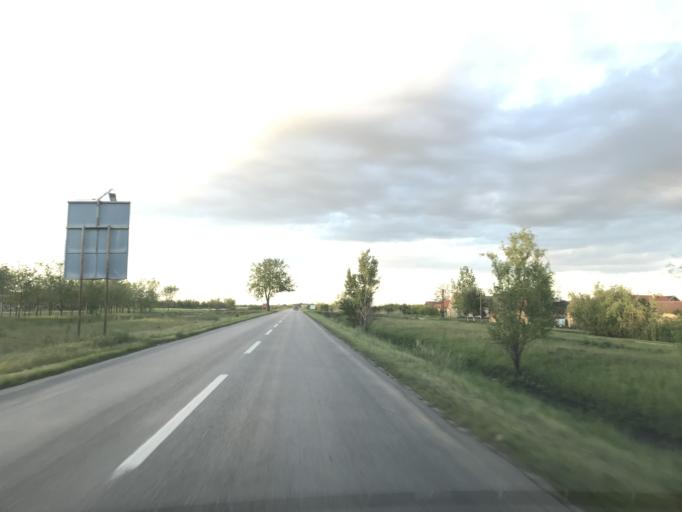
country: RS
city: Banatsko Karadordevo
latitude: 45.5954
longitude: 20.5598
